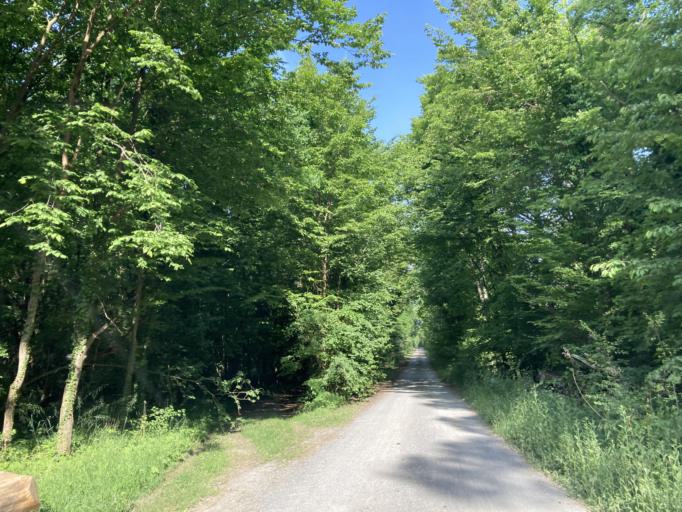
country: DE
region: Baden-Wuerttemberg
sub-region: Karlsruhe Region
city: Kronau
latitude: 49.2015
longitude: 8.5971
